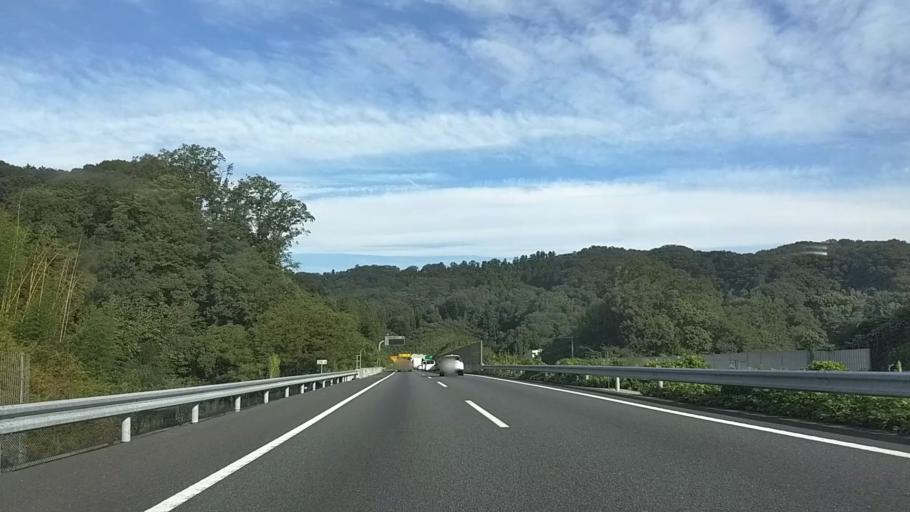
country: JP
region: Kanagawa
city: Zama
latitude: 35.5562
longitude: 139.3147
